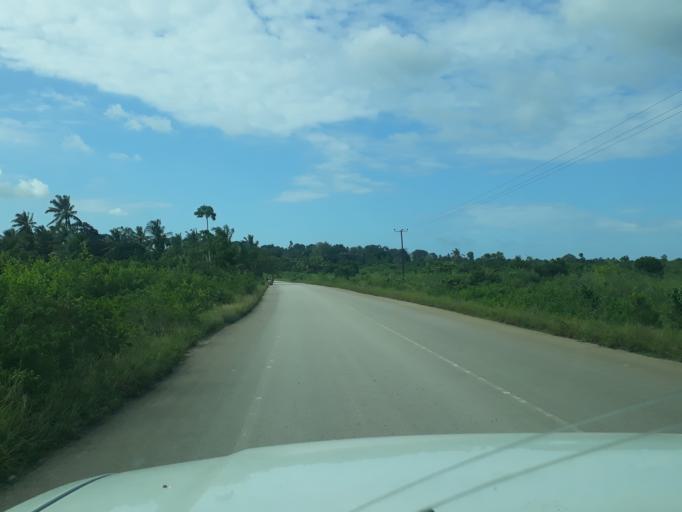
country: TZ
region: Zanzibar North
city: Kijini
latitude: -5.8364
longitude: 39.2886
